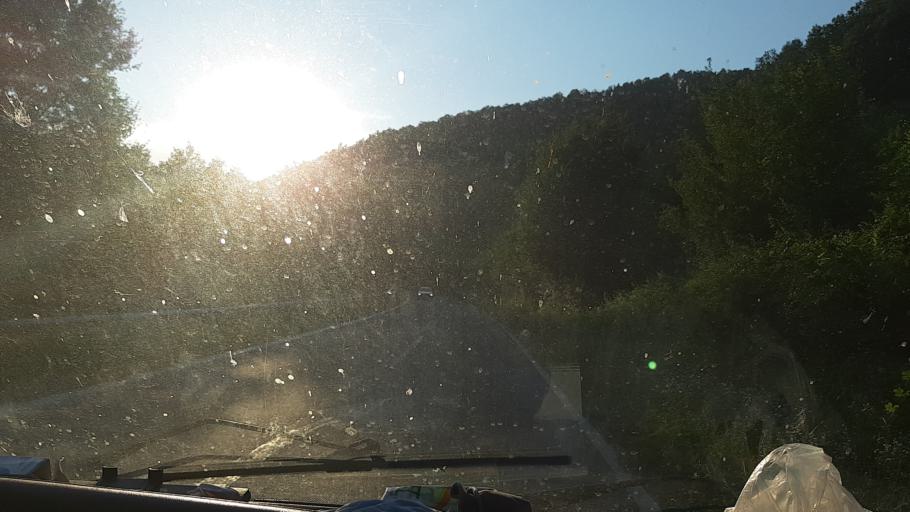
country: RO
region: Caras-Severin
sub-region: Municipiul Resita
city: Calnic
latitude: 45.3543
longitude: 21.8299
